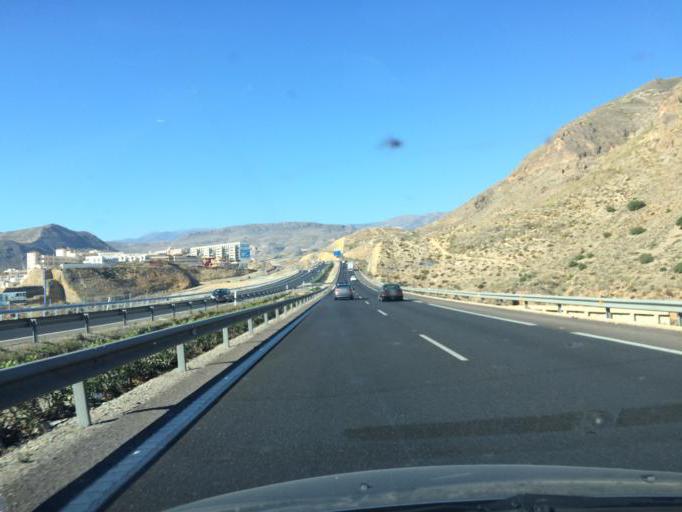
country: ES
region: Andalusia
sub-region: Provincia de Almeria
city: Aguadulce
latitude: 36.8241
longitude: -2.5778
